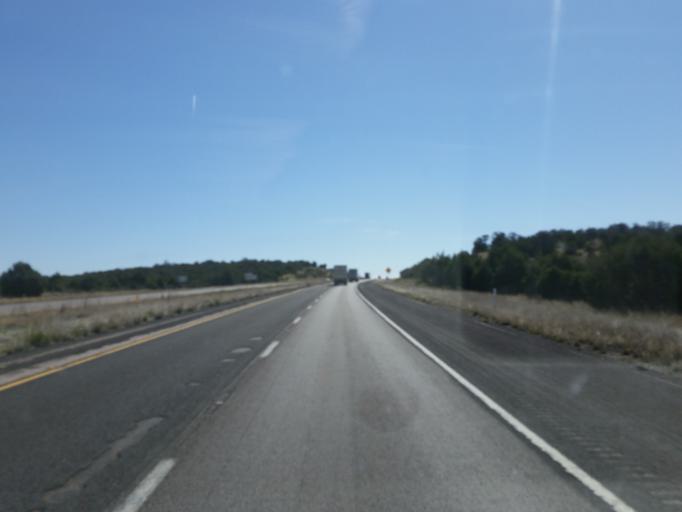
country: US
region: Arizona
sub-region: Mohave County
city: Peach Springs
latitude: 35.2899
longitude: -113.0854
